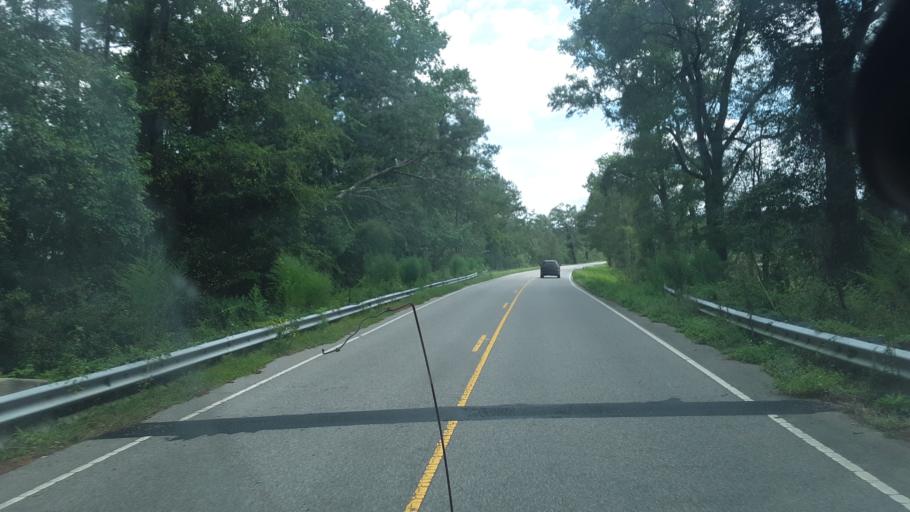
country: US
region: North Carolina
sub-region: Robeson County
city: Fairmont
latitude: 34.3437
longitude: -79.0682
